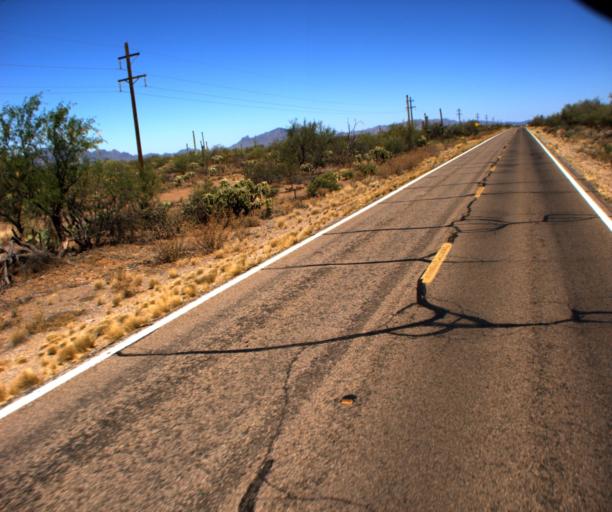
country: US
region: Arizona
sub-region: Pima County
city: Sells
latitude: 31.9762
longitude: -111.9650
